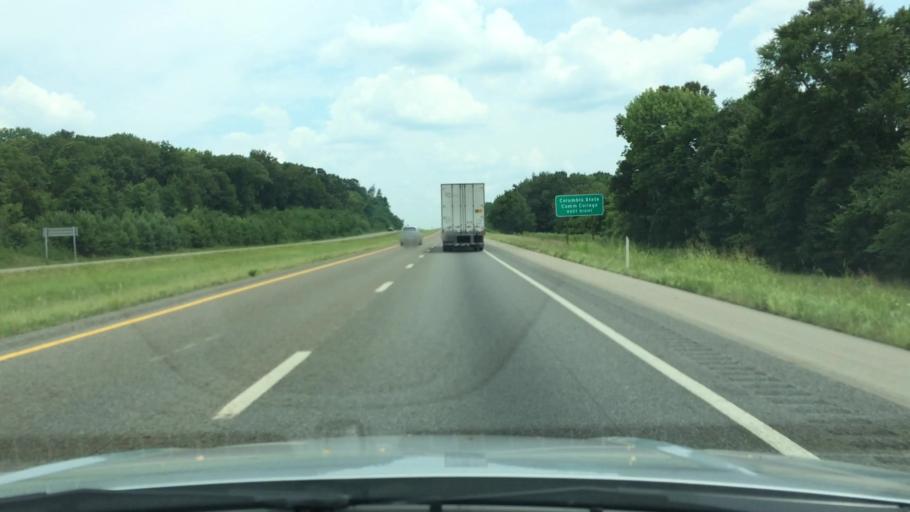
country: US
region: Tennessee
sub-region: Maury County
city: Spring Hill
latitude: 35.6299
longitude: -86.8964
